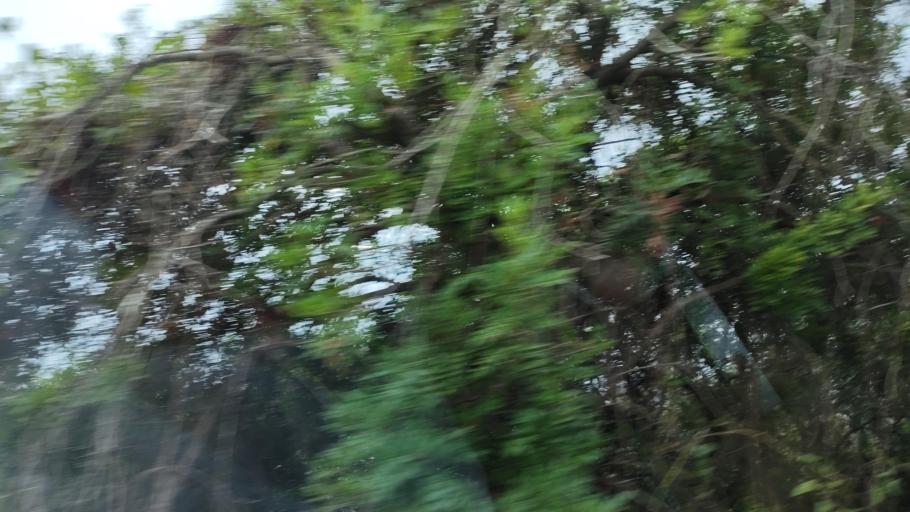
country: GI
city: Gibraltar
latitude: 36.1247
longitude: -5.3464
